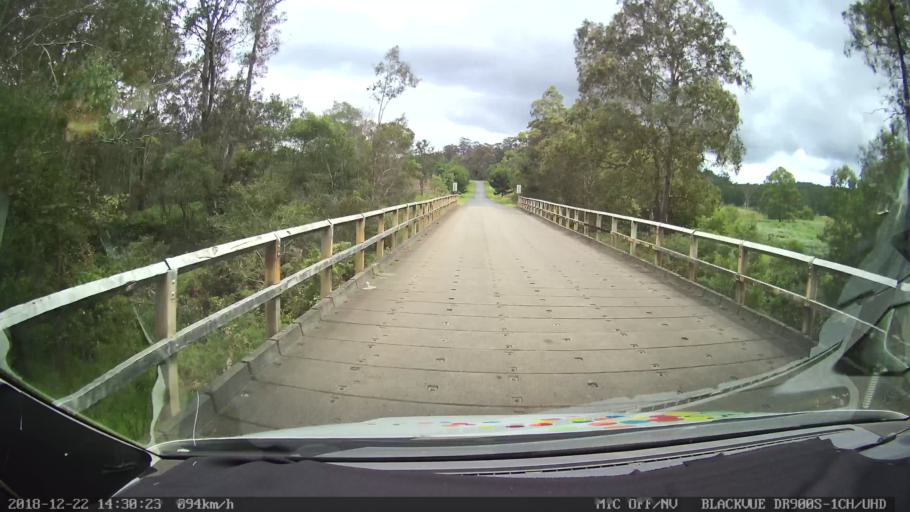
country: AU
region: New South Wales
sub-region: Bellingen
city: Dorrigo
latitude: -30.0857
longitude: 152.6317
